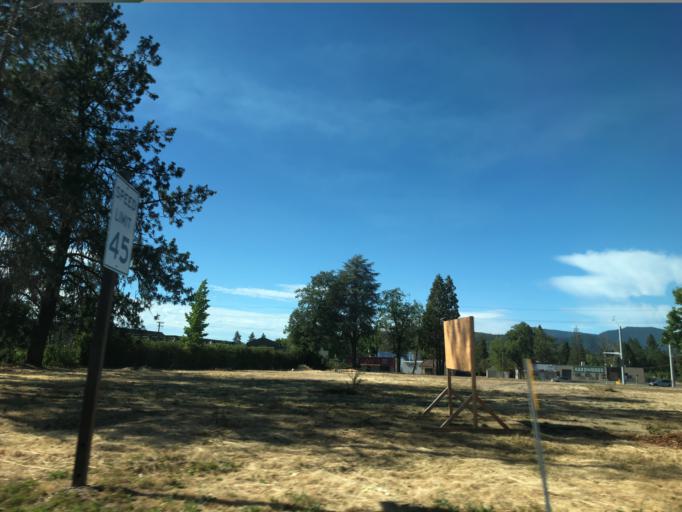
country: US
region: Oregon
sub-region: Josephine County
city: Grants Pass
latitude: 42.4214
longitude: -123.3519
